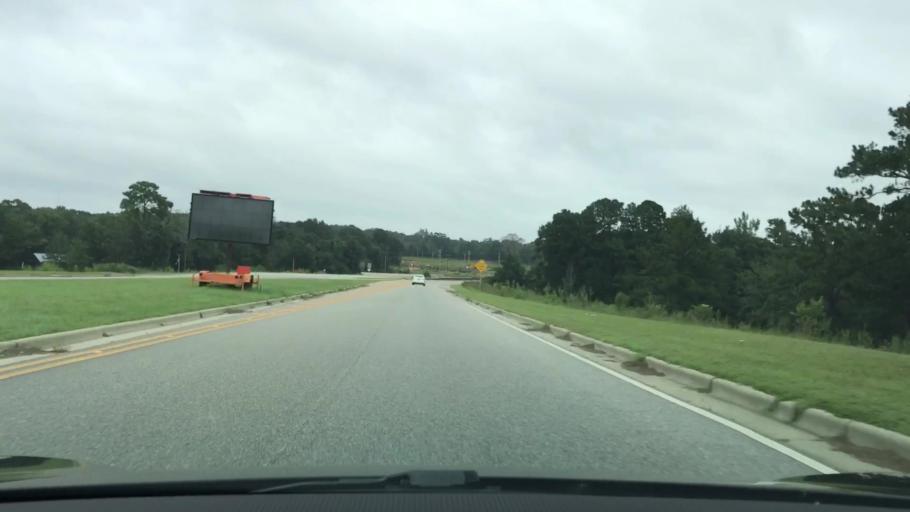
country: US
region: Alabama
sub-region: Coffee County
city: Elba
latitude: 31.4194
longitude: -86.0867
